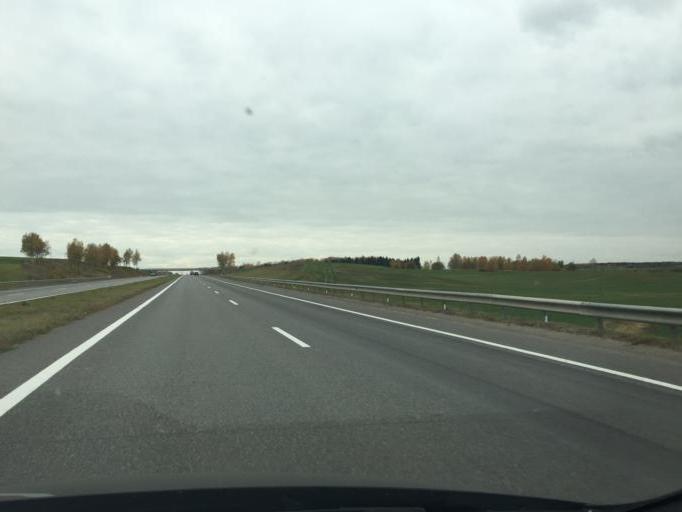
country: BY
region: Minsk
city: Samakhvalavichy
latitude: 53.7169
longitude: 27.4829
